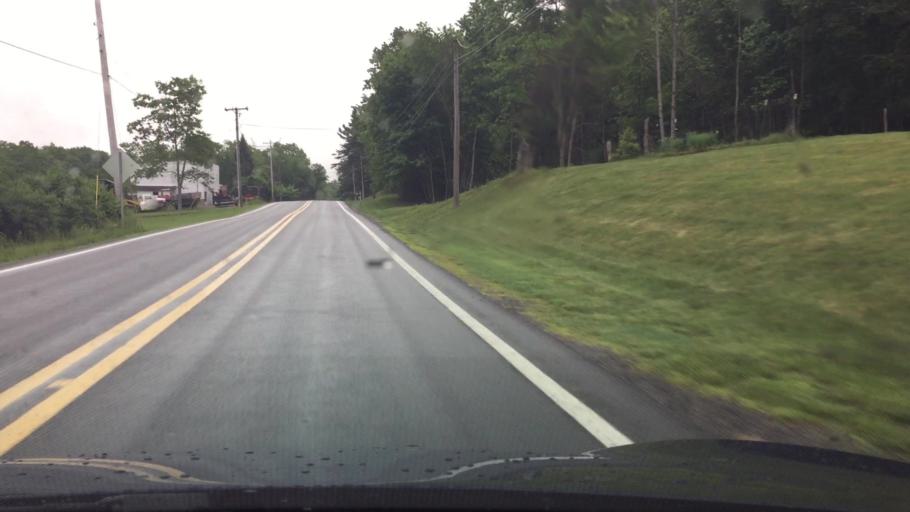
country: US
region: West Virginia
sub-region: Raleigh County
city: Shady Spring
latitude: 37.6915
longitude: -81.0640
